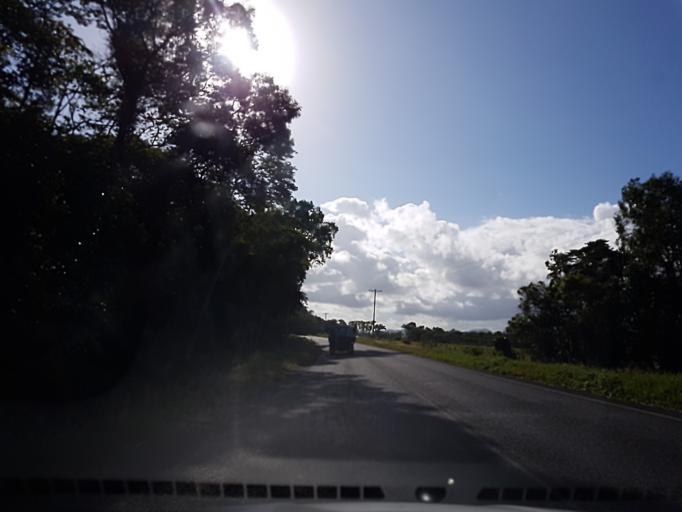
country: AU
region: Queensland
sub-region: Cairns
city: Port Douglas
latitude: -16.3213
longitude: 145.4070
